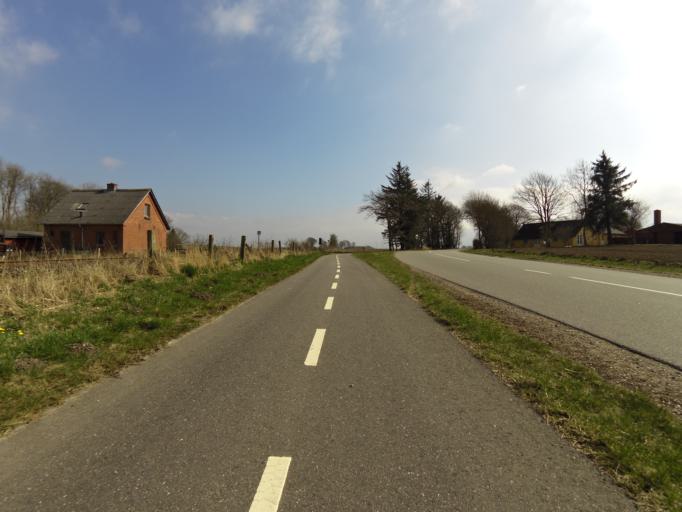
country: DK
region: Central Jutland
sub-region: Struer Kommune
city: Struer
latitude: 56.4499
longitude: 8.6213
